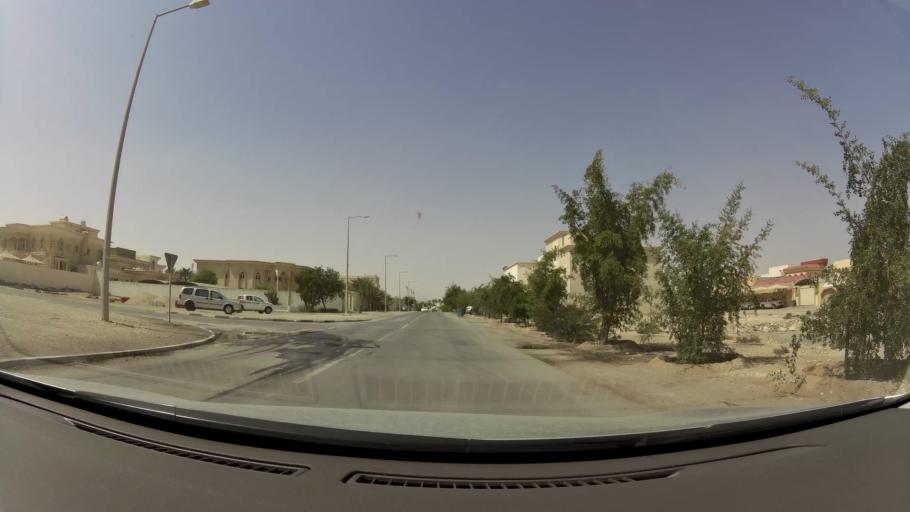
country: QA
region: Baladiyat Umm Salal
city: Umm Salal Muhammad
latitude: 25.3774
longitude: 51.4256
